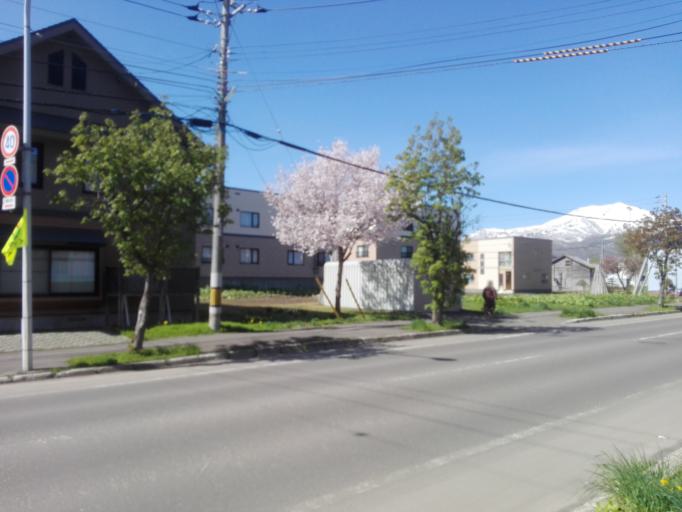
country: JP
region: Hokkaido
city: Niseko Town
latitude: 42.8989
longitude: 140.7566
